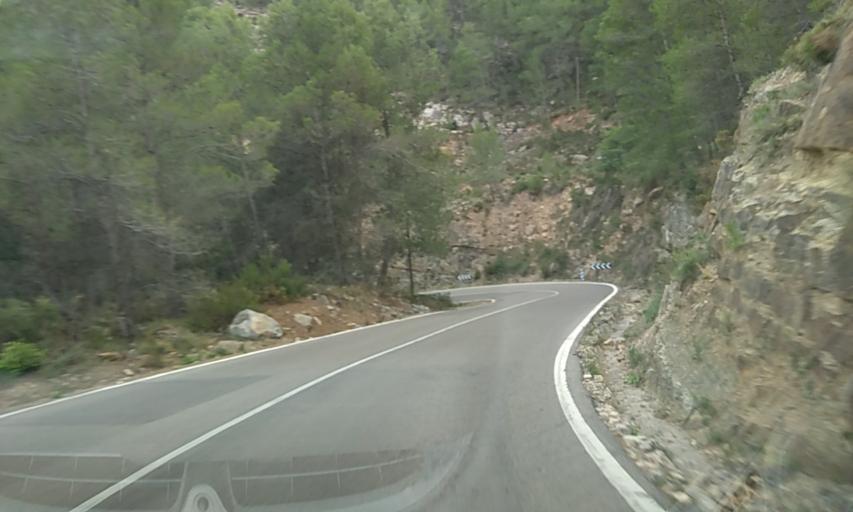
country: ES
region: Valencia
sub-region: Provincia de Castello
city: Montanejos
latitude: 40.0828
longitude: -0.5463
